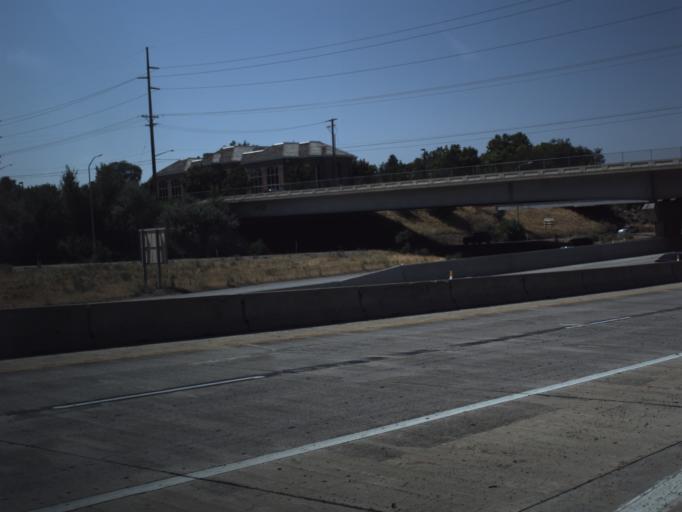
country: US
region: Utah
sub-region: Salt Lake County
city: Midvale
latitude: 40.6305
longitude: -111.8648
